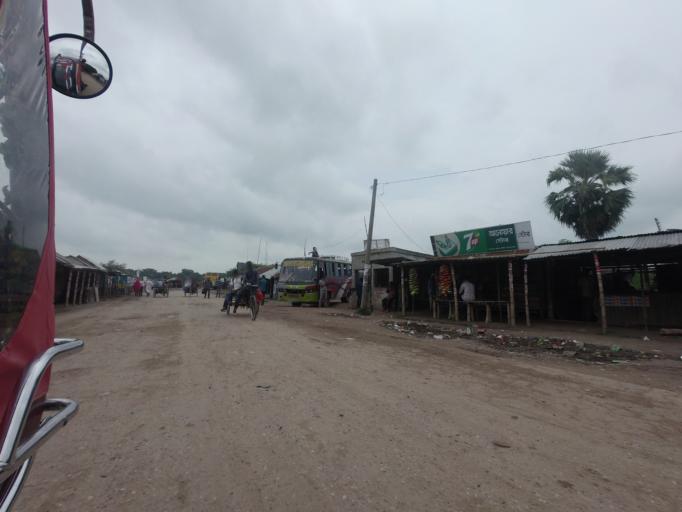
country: BD
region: Khulna
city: Kalia
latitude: 23.1947
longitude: 89.6884
